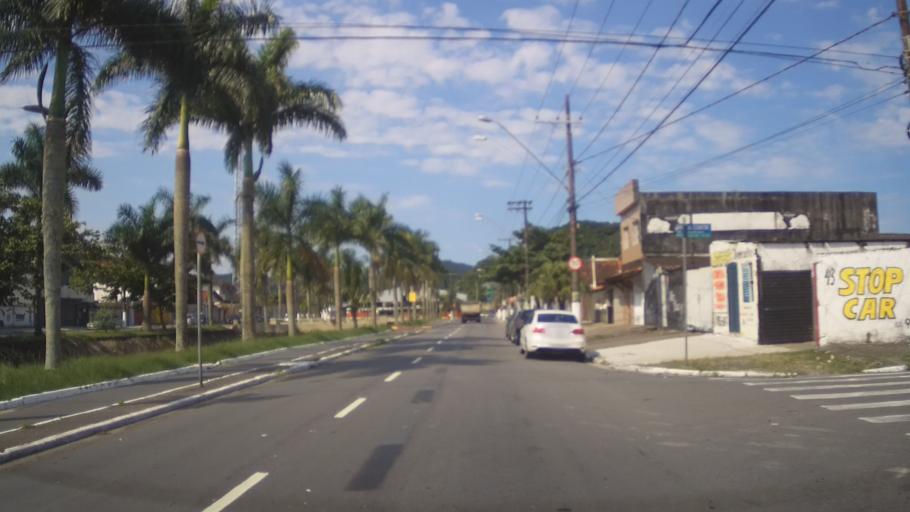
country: BR
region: Sao Paulo
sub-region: Praia Grande
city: Praia Grande
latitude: -23.9997
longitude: -46.4174
